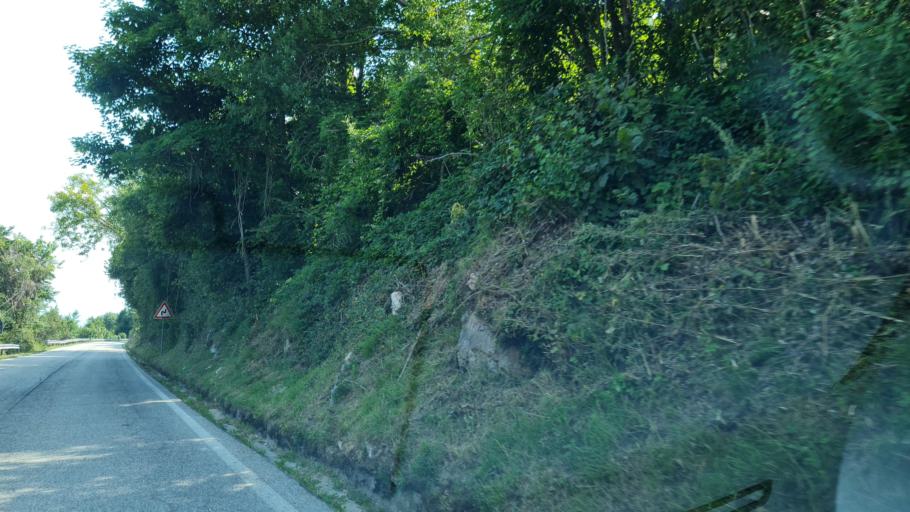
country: IT
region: Veneto
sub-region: Provincia di Vicenza
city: Conco
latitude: 45.7997
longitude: 11.6536
